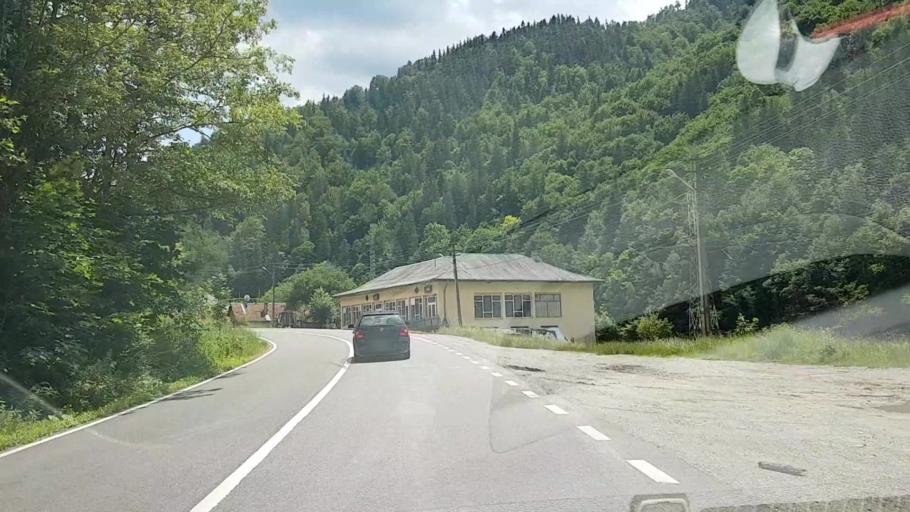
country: RO
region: Suceava
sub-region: Comuna Crucea
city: Crucea
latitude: 47.2843
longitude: 25.6366
